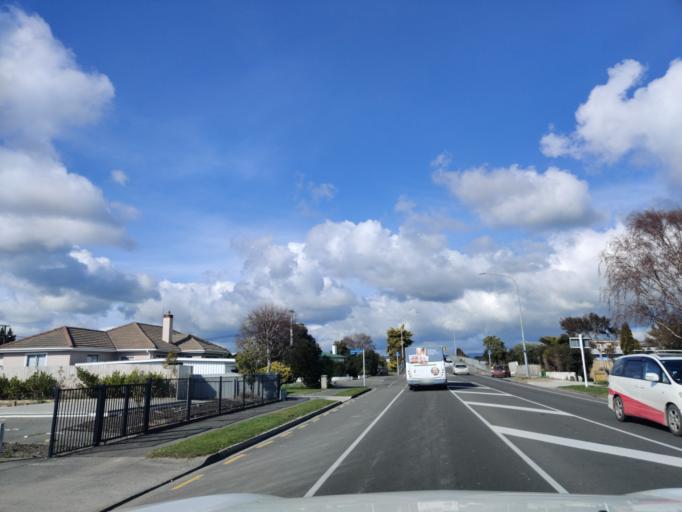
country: NZ
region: Manawatu-Wanganui
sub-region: Palmerston North City
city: Palmerston North
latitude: -40.3321
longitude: 175.6156
